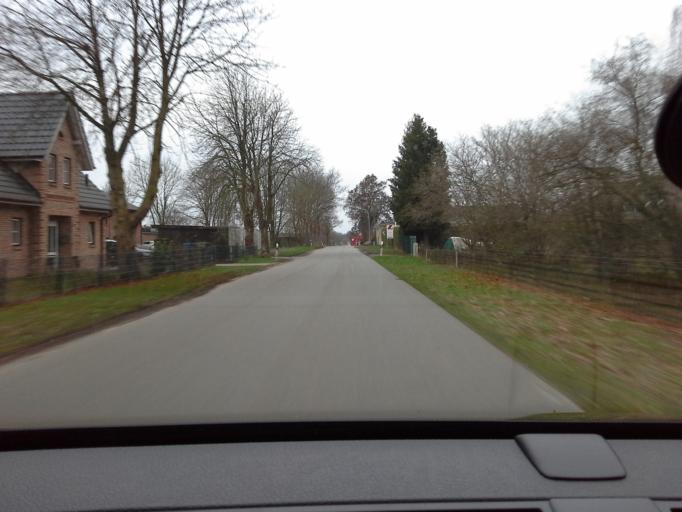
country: DE
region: Schleswig-Holstein
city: Lentfohrden
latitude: 53.8658
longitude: 9.8755
